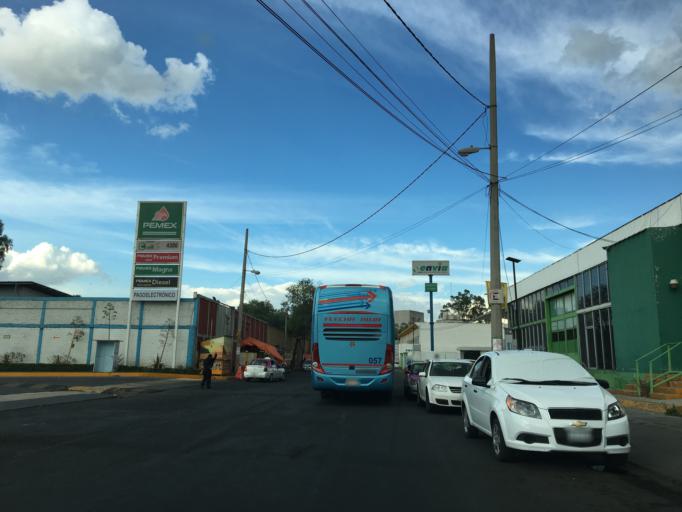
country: MX
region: Mexico
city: Colonia Lindavista
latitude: 19.4812
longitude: -99.1395
